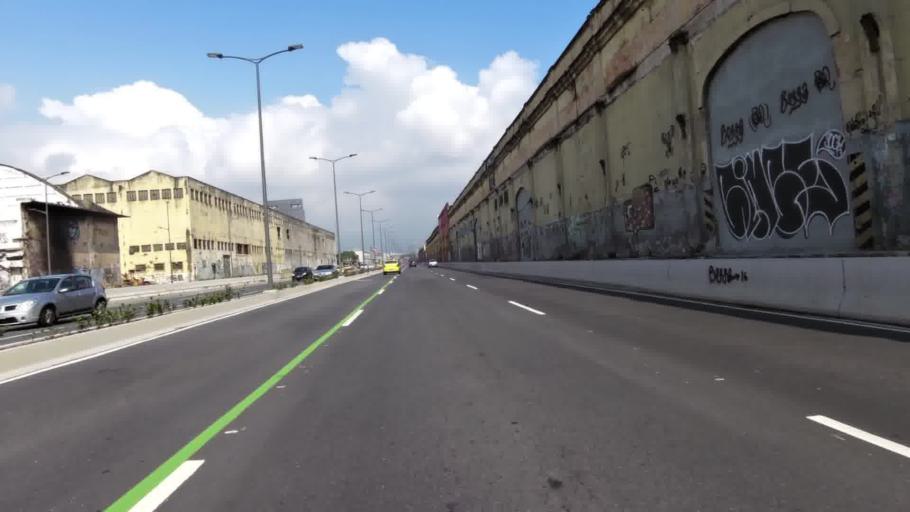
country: BR
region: Rio de Janeiro
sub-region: Rio De Janeiro
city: Rio de Janeiro
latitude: -22.8948
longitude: -43.2011
